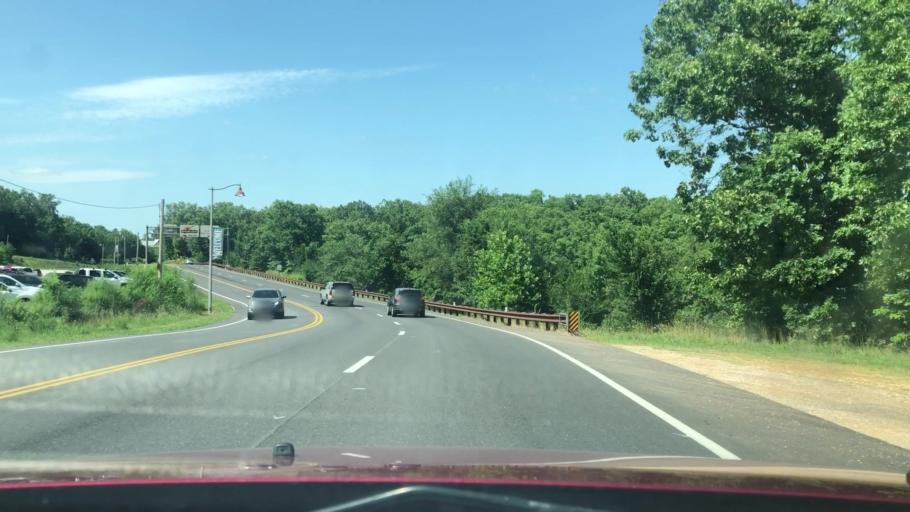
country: US
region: Missouri
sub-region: Stone County
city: Kimberling City
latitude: 36.6634
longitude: -93.3367
